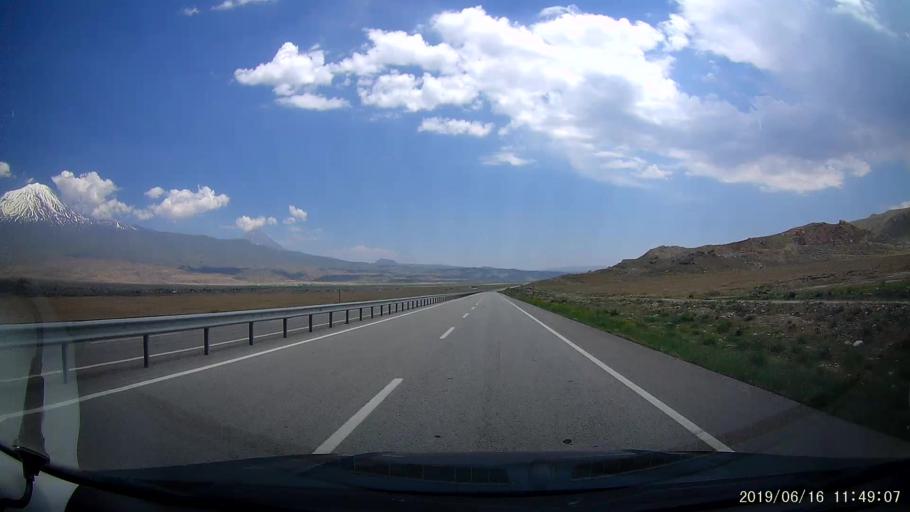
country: TR
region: Agri
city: Dogubayazit
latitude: 39.5578
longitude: 44.1571
